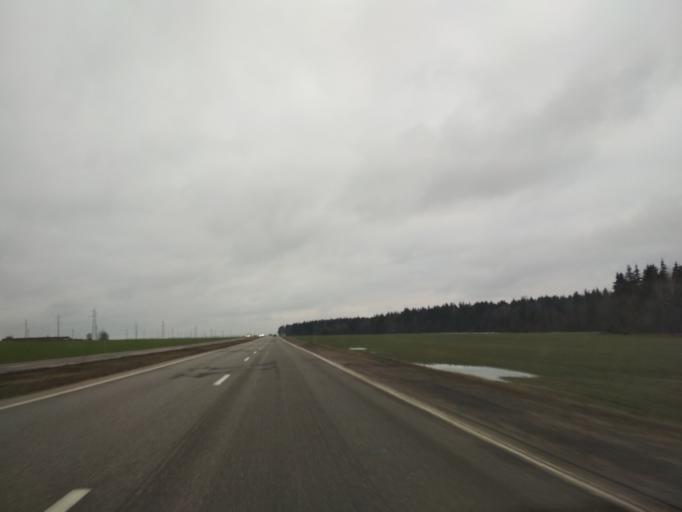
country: BY
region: Minsk
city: Dukora
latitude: 53.6162
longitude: 28.0564
